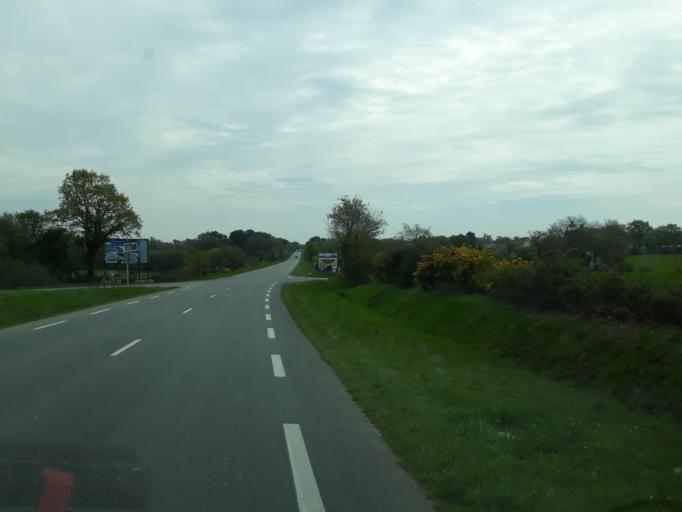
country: FR
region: Brittany
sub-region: Departement du Morbihan
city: Marzan
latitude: 47.5261
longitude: -2.3810
